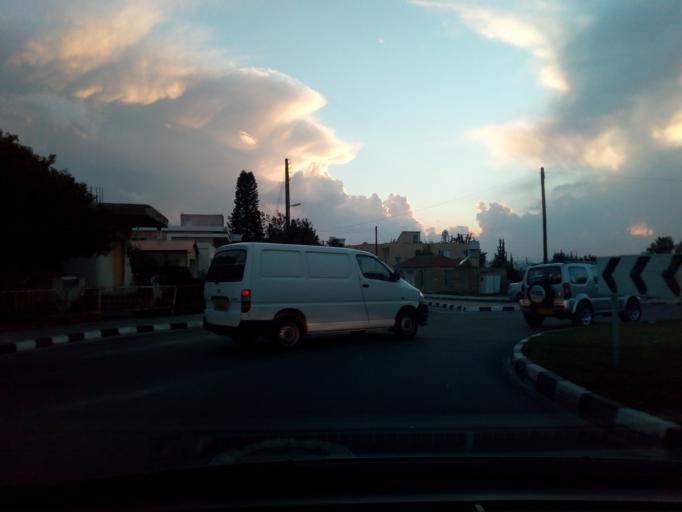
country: CY
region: Pafos
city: Paphos
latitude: 34.7751
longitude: 32.4367
